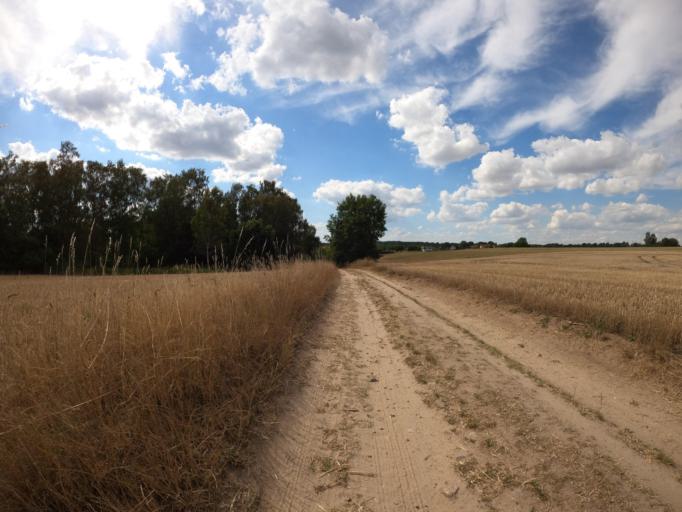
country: DE
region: Mecklenburg-Vorpommern
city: Loitz
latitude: 53.3155
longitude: 13.4216
